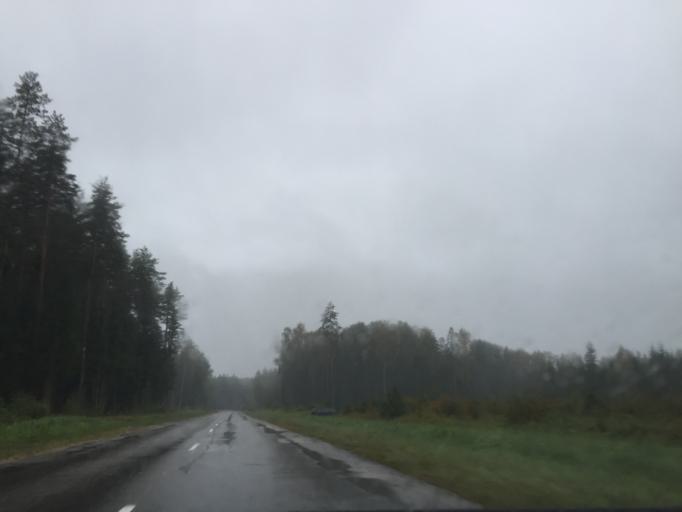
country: LV
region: Ropazu
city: Ropazi
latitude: 57.0143
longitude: 24.6818
